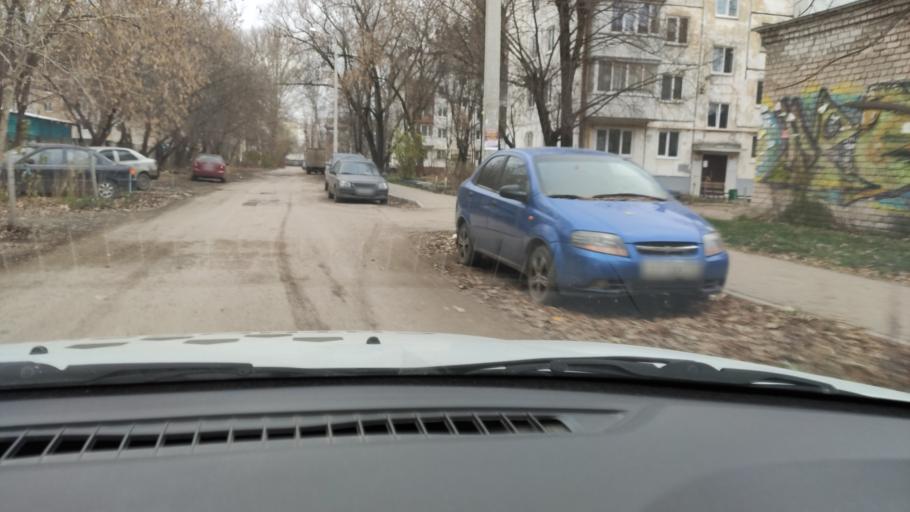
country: RU
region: Perm
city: Perm
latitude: 58.0109
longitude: 56.2876
